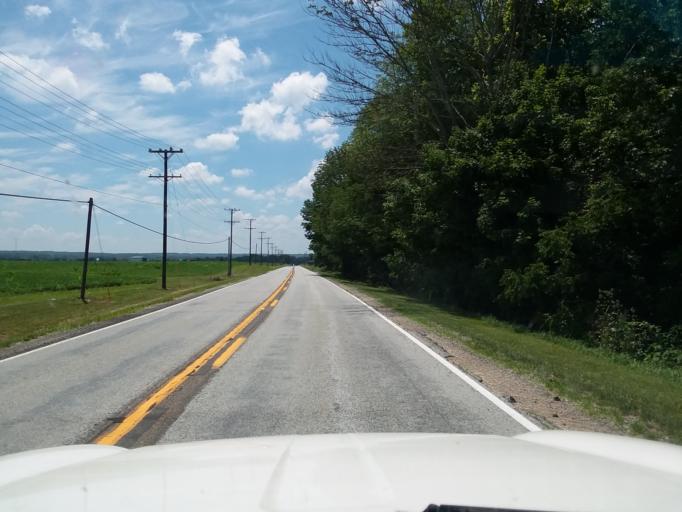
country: US
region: Indiana
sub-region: Johnson County
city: Trafalgar
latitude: 39.3822
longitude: -86.2415
